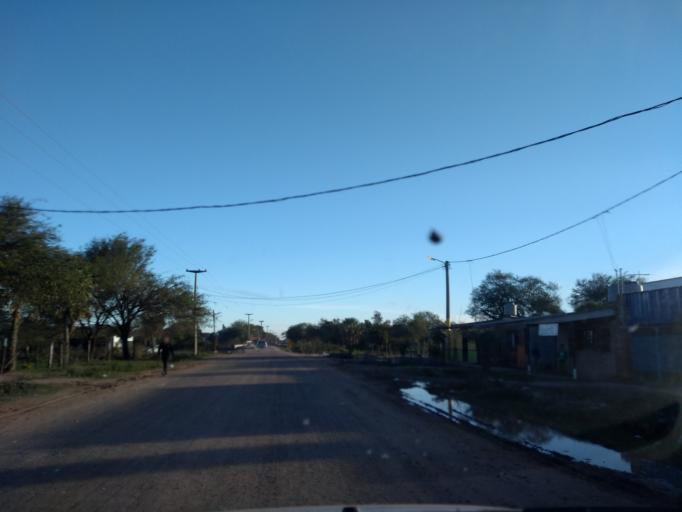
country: AR
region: Chaco
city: Puerto Vilelas
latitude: -27.4975
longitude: -58.9668
